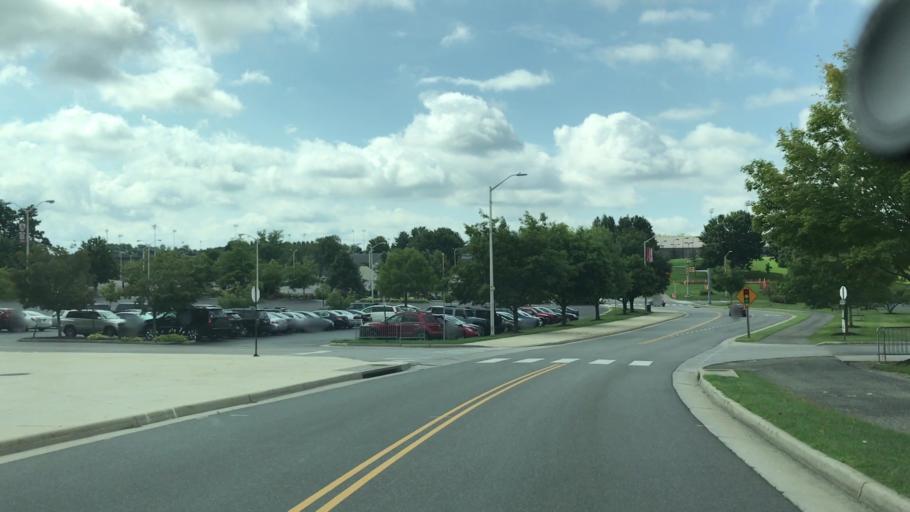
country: US
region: Virginia
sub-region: Montgomery County
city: Blacksburg
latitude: 37.2189
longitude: -80.4193
